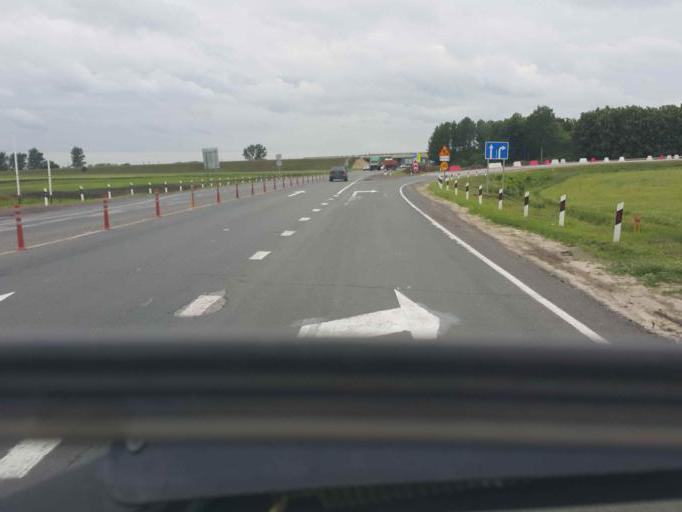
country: RU
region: Tambov
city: Zavoronezhskoye
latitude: 52.9080
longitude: 40.6377
